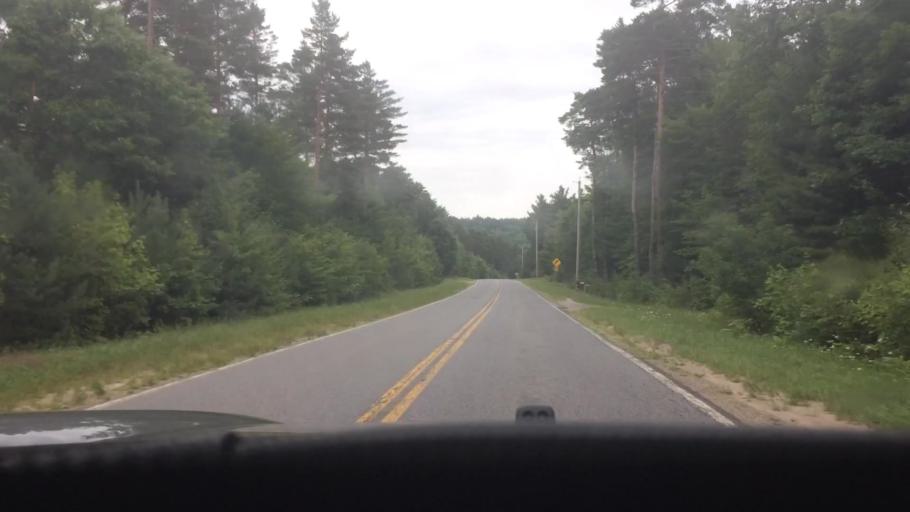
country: US
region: New York
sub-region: St. Lawrence County
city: Hannawa Falls
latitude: 44.5598
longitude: -74.9259
